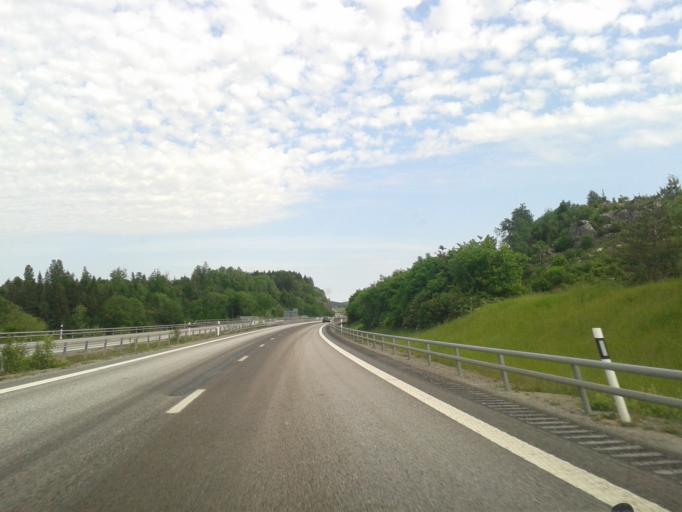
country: SE
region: Vaestra Goetaland
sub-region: Munkedals Kommun
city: Munkedal
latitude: 58.4927
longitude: 11.5752
